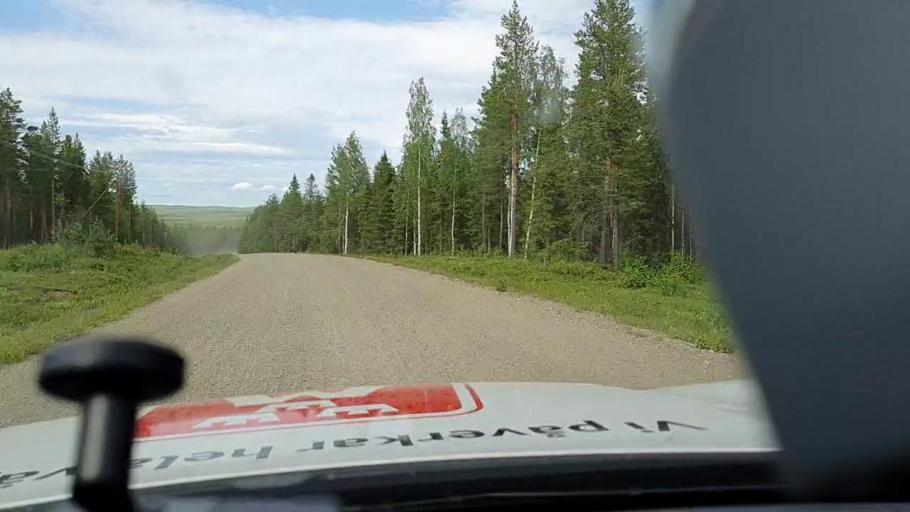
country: SE
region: Norrbotten
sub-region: Alvsbyns Kommun
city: AElvsbyn
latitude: 66.1422
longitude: 21.0169
